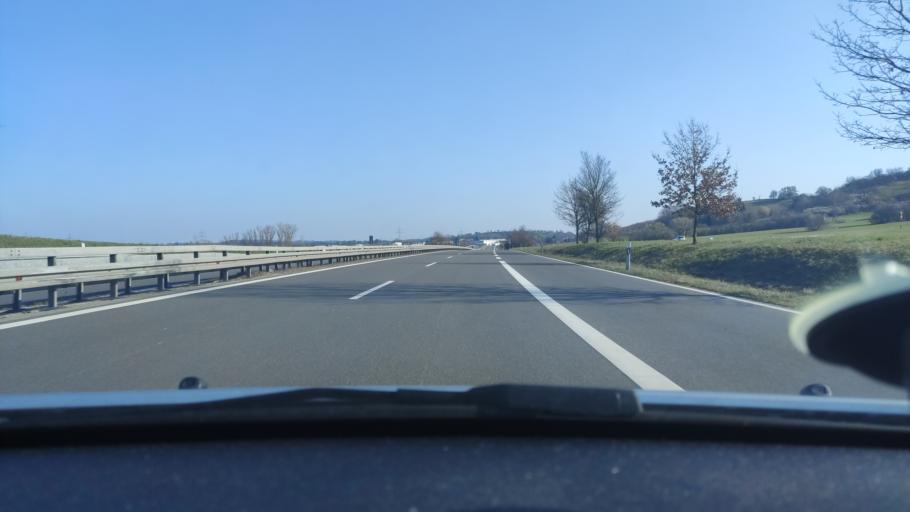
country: DE
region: Baden-Wuerttemberg
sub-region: Tuebingen Region
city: Balingen
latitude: 48.2856
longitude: 8.8626
